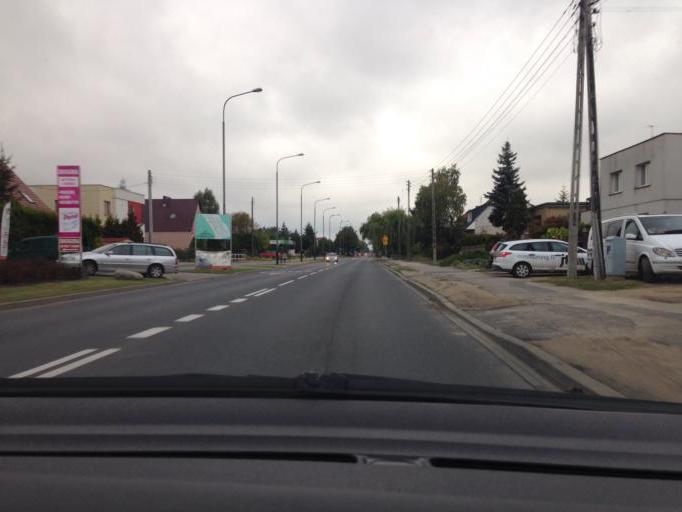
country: PL
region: Greater Poland Voivodeship
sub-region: Powiat poznanski
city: Suchy Las
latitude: 52.4515
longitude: 16.8887
